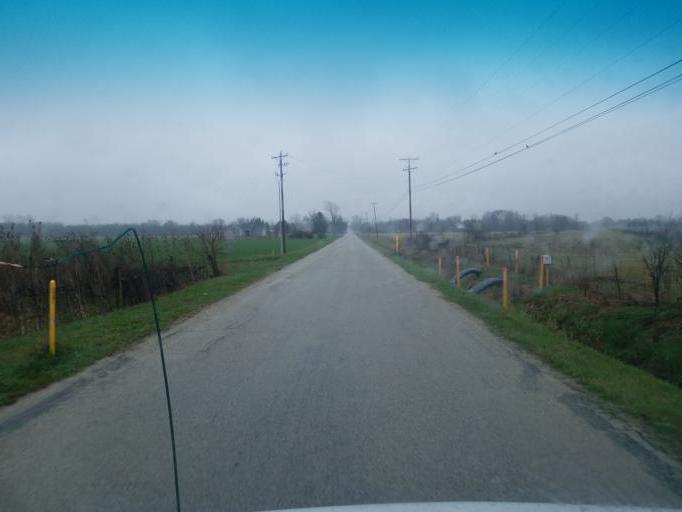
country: US
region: Ohio
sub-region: Wood County
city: North Baltimore
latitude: 41.2511
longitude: -83.6308
